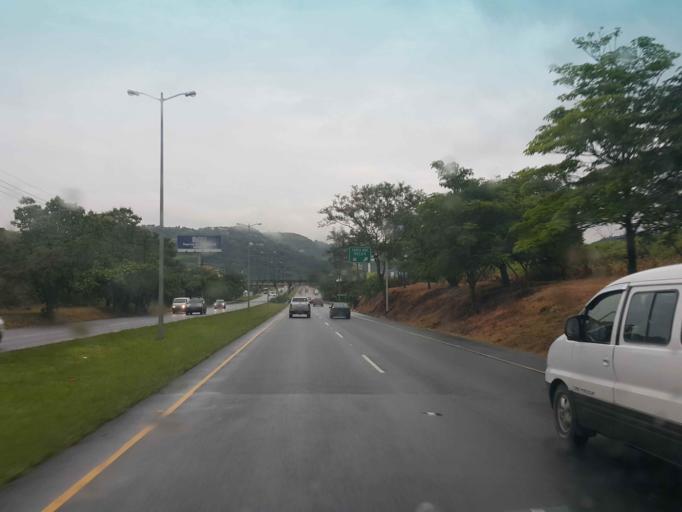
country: CR
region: San Jose
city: Santa Ana
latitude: 9.9422
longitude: -84.1963
